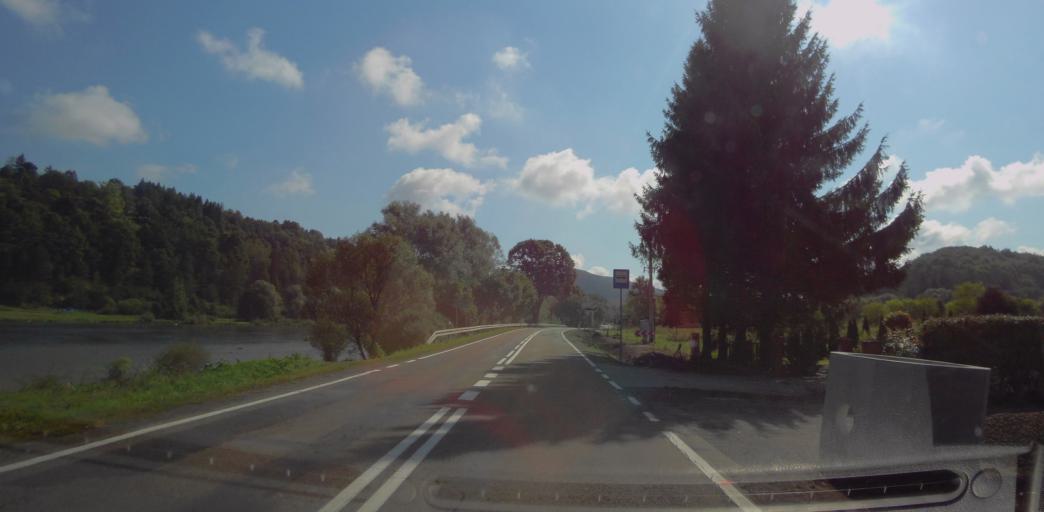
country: PL
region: Subcarpathian Voivodeship
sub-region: Powiat leski
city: Lesko
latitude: 49.4640
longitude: 22.3256
